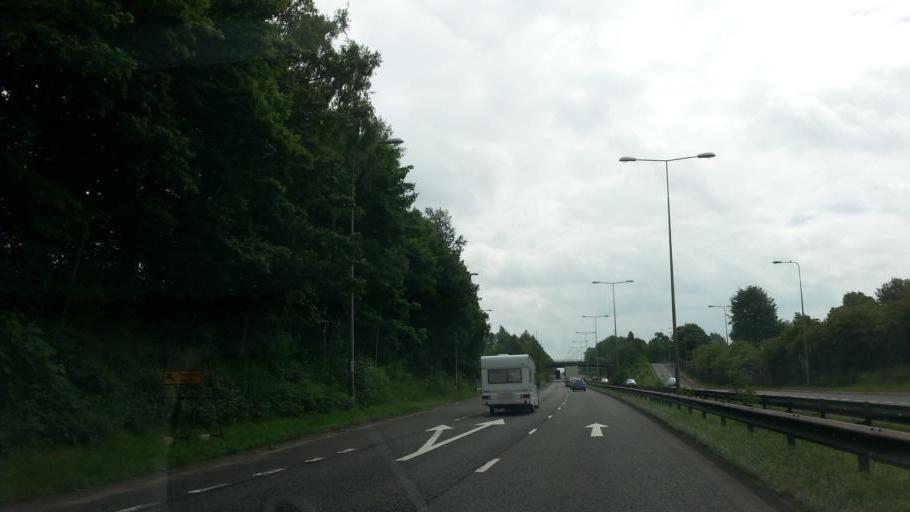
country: GB
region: England
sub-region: Staffordshire
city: Longton
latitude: 52.9685
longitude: -2.0814
